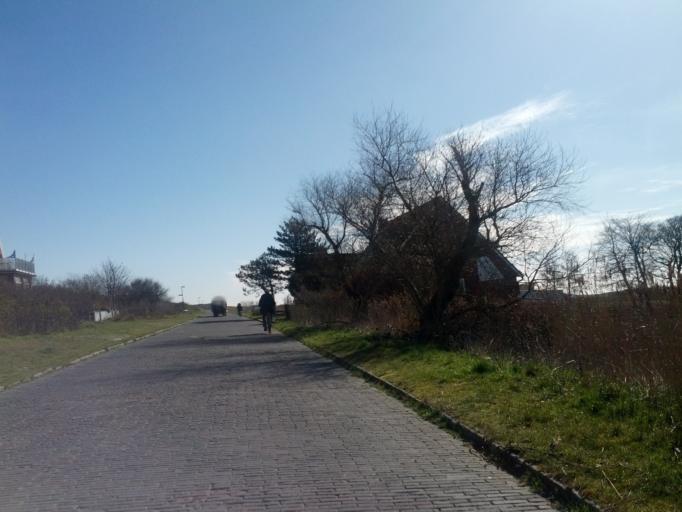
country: DE
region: Lower Saxony
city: Langeoog
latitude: 53.7505
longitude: 7.4895
